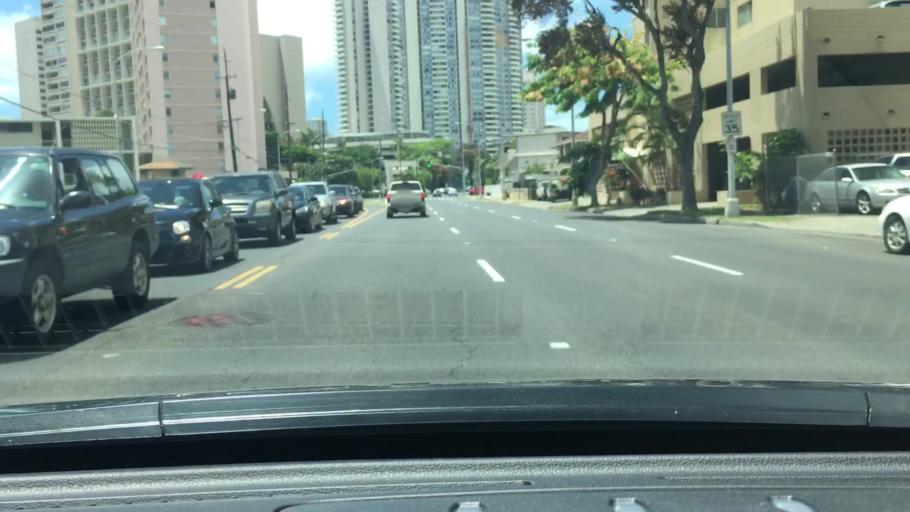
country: US
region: Hawaii
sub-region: Honolulu County
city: Honolulu
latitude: 21.2876
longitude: -157.8243
